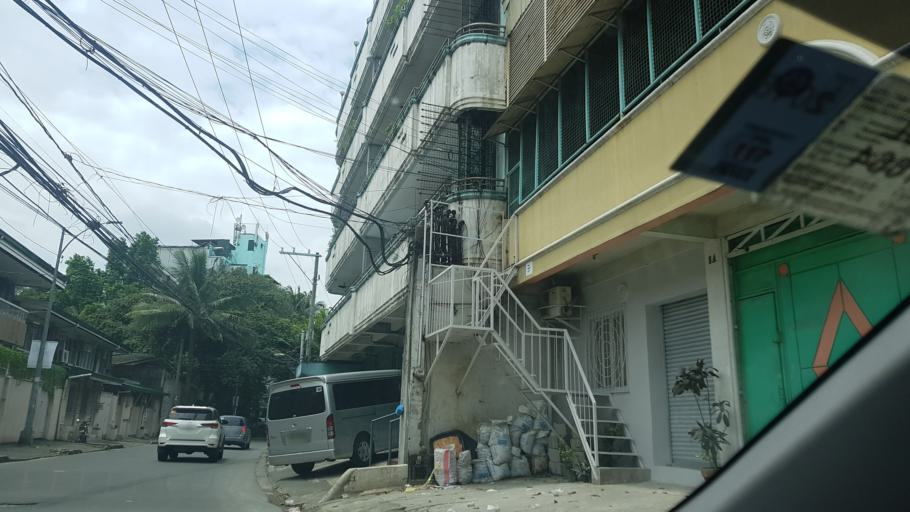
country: PH
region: Calabarzon
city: Del Monte
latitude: 14.6504
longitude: 121.0042
